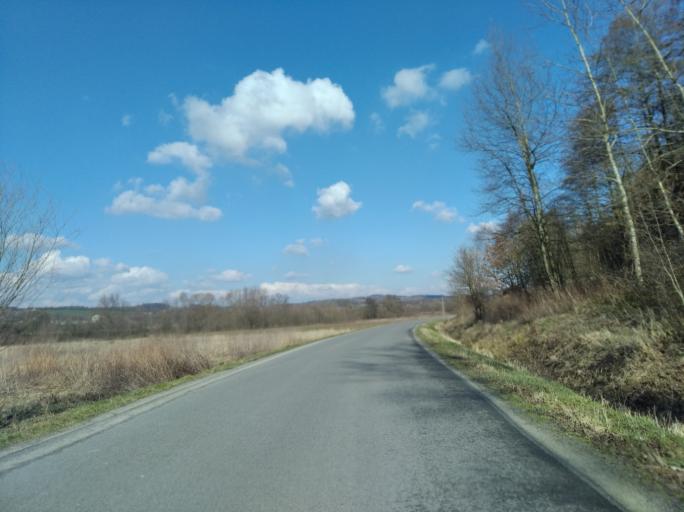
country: PL
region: Subcarpathian Voivodeship
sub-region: Powiat strzyzowski
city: Frysztak
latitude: 49.8543
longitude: 21.6250
